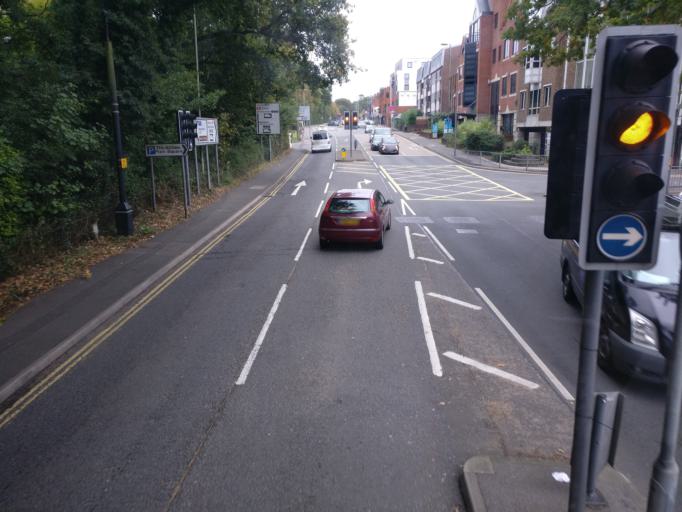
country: GB
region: England
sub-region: Surrey
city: Camberley
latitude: 51.3387
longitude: -0.7508
